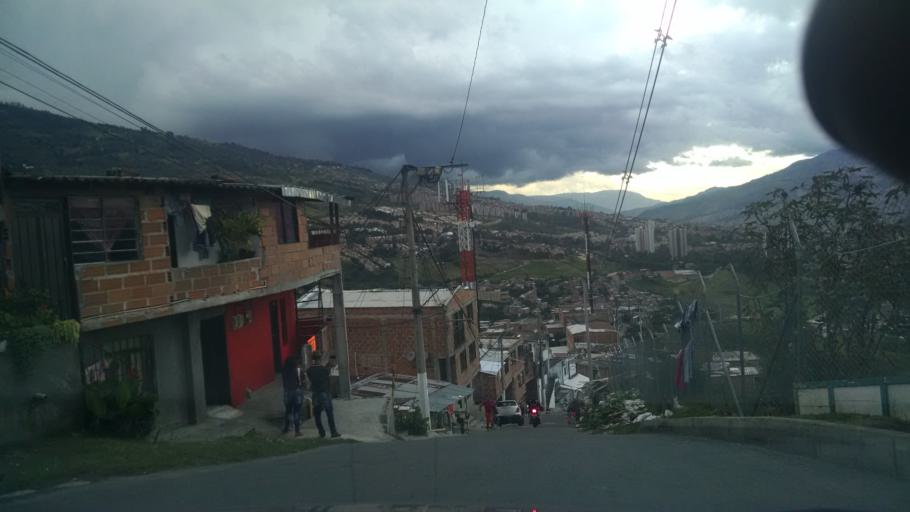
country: CO
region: Antioquia
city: Medellin
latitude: 6.2712
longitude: -75.6128
